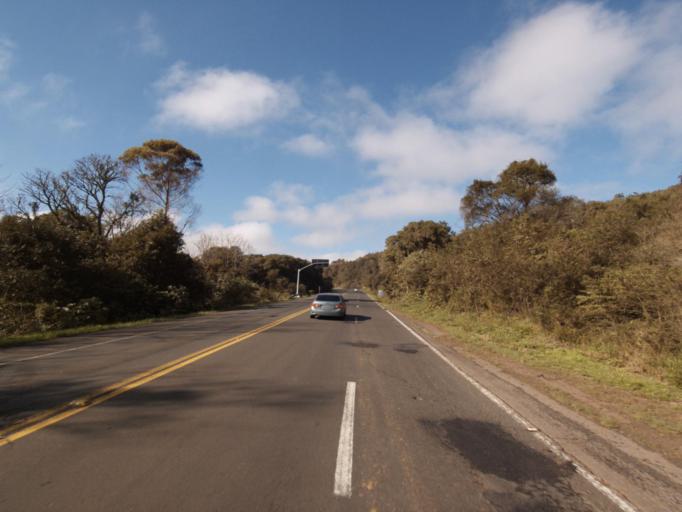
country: BR
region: Rio Grande do Sul
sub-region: Frederico Westphalen
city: Frederico Westphalen
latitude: -27.0811
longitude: -53.2239
